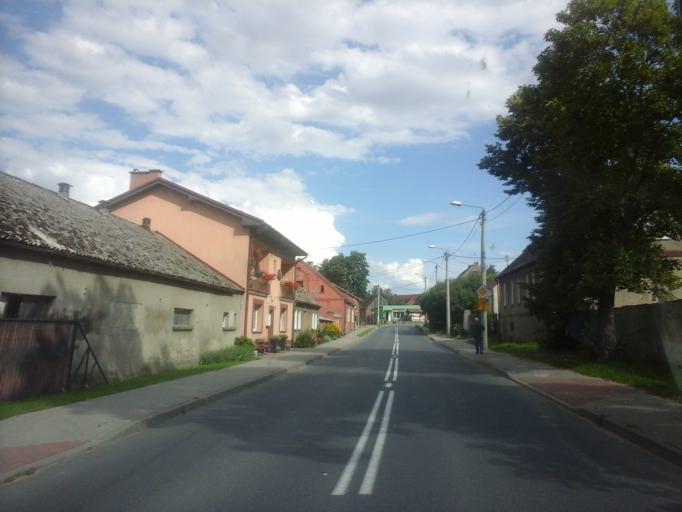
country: PL
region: West Pomeranian Voivodeship
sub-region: Powiat stargardzki
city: Suchan
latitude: 53.2277
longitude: 15.2991
